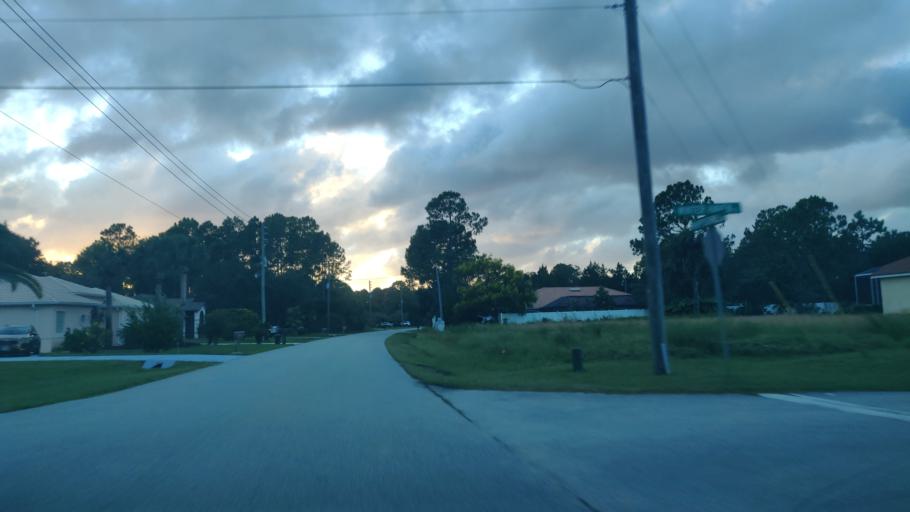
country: US
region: Florida
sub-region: Flagler County
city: Bunnell
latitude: 29.5214
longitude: -81.2281
